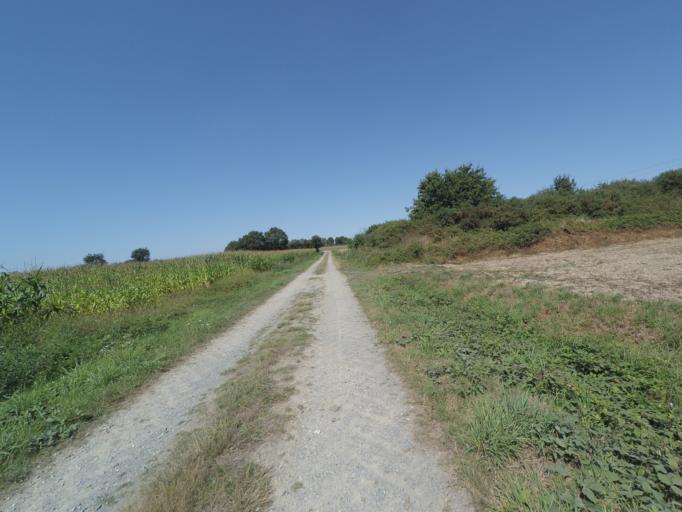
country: FR
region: Pays de la Loire
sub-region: Departement de la Loire-Atlantique
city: La Planche
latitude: 46.9976
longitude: -1.4137
